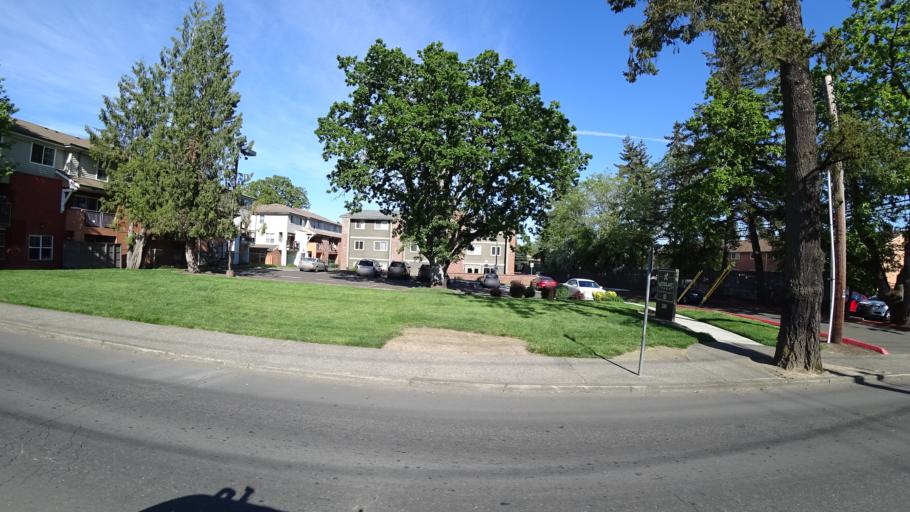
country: US
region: Oregon
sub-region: Washington County
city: Hillsboro
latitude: 45.5201
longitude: -122.9702
